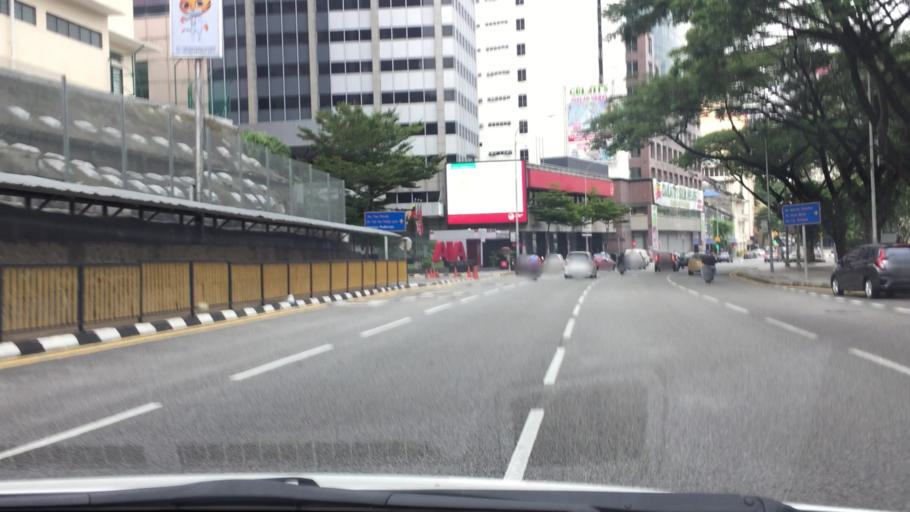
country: MY
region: Kuala Lumpur
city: Kuala Lumpur
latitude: 3.1529
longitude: 101.7002
